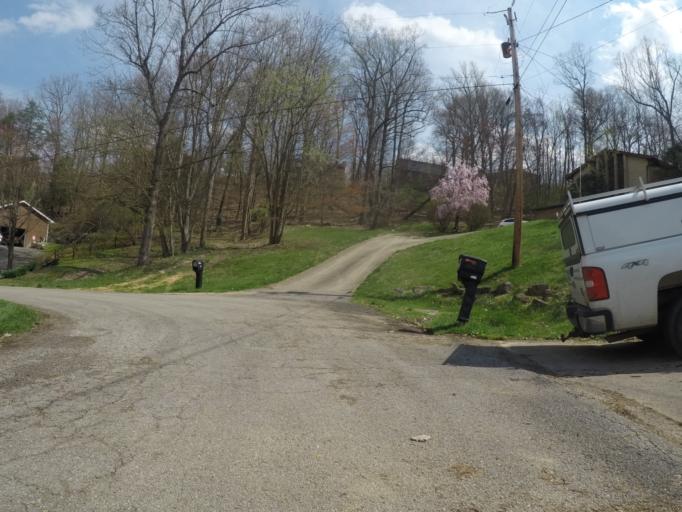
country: US
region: West Virginia
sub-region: Cabell County
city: Pea Ridge
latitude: 38.4004
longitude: -82.3339
